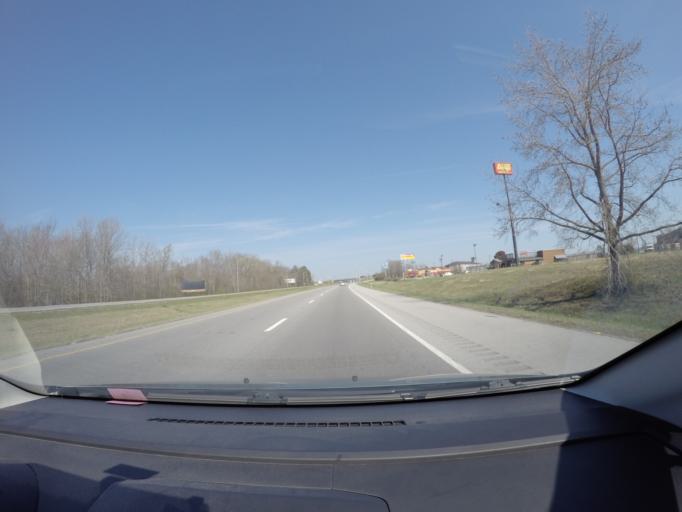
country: US
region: Tennessee
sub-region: Coffee County
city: Manchester
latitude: 35.4520
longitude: -86.0491
